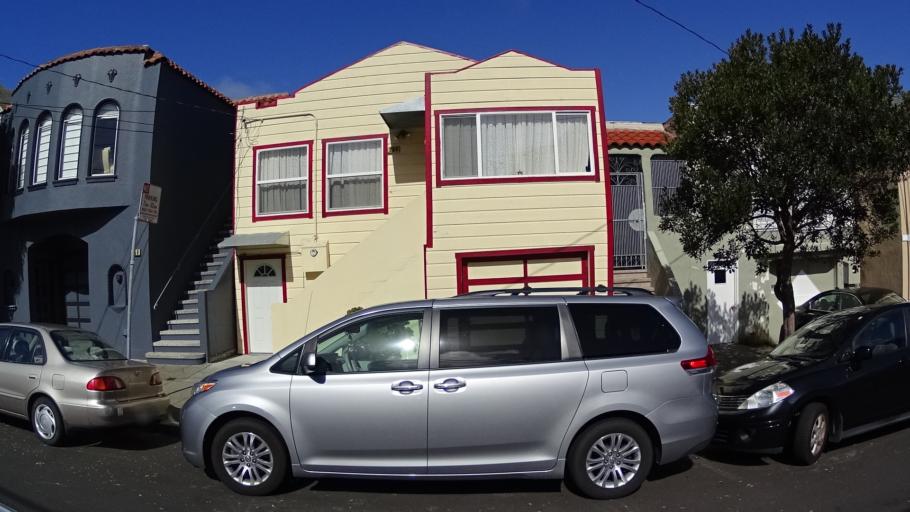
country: US
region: California
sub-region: San Mateo County
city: Daly City
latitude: 37.7071
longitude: -122.4554
